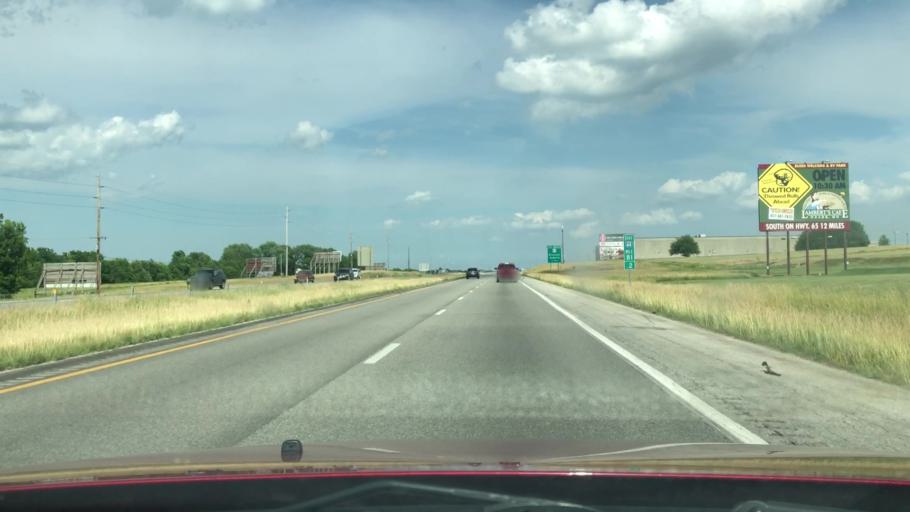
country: US
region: Missouri
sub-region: Greene County
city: Springfield
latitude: 37.2501
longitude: -93.2486
